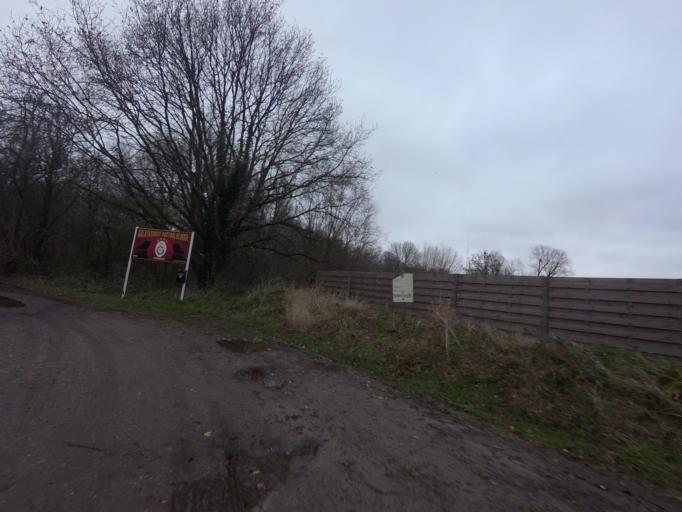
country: BE
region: Flanders
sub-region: Provincie Antwerpen
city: Hoboken
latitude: 51.1619
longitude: 4.3487
